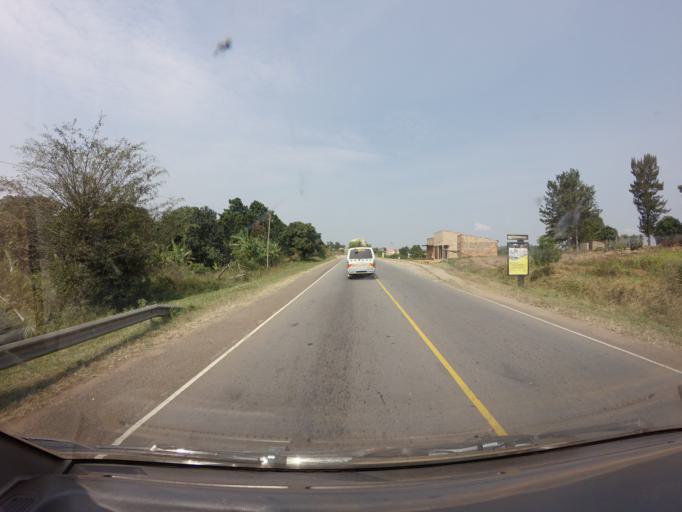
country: UG
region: Central Region
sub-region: Lwengo District
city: Lwengo
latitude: -0.3983
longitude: 31.4023
